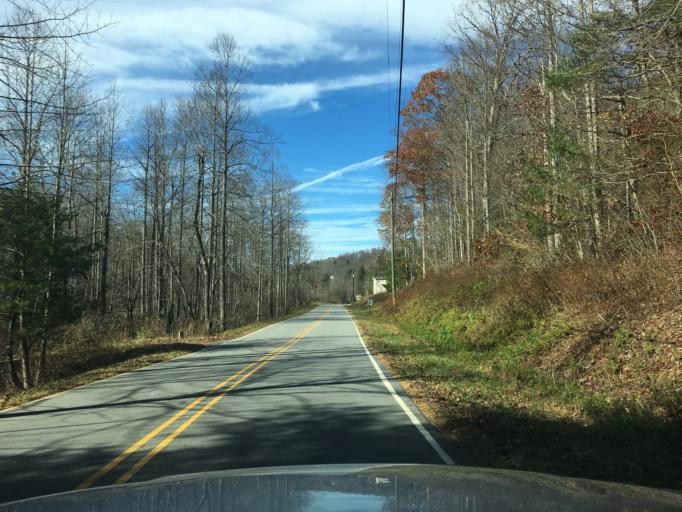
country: US
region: North Carolina
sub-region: Henderson County
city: Flat Rock
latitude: 35.2252
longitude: -82.4976
